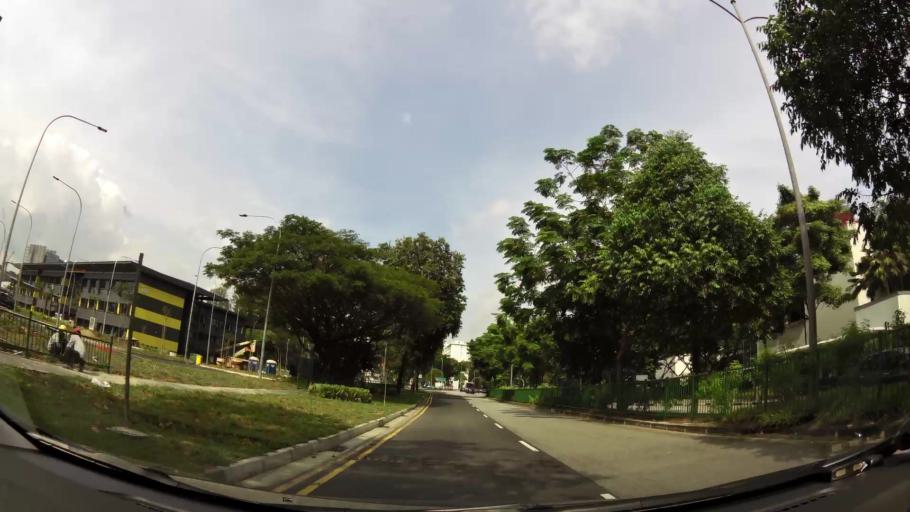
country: SG
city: Singapore
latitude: 1.2988
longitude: 103.7868
